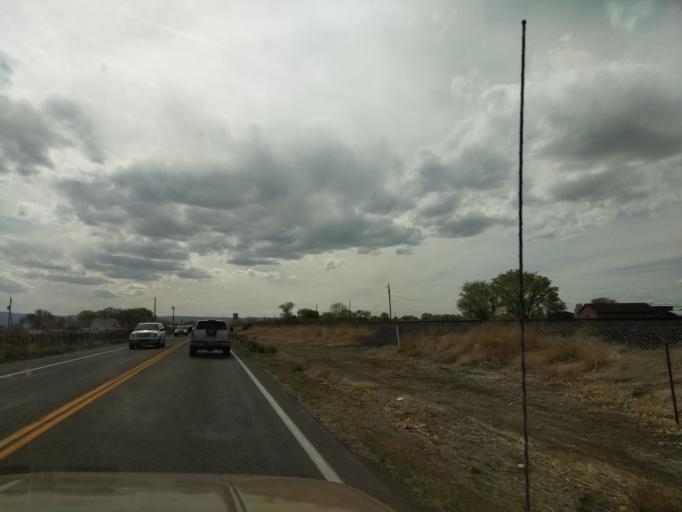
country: US
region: Colorado
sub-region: Mesa County
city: Clifton
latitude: 39.0969
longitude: -108.4105
